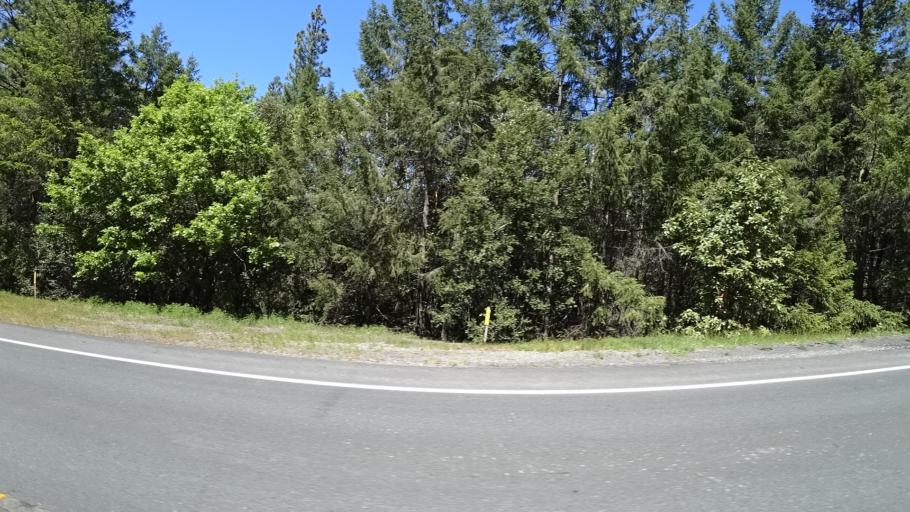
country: US
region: California
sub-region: Humboldt County
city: Willow Creek
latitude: 40.8495
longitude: -123.4857
